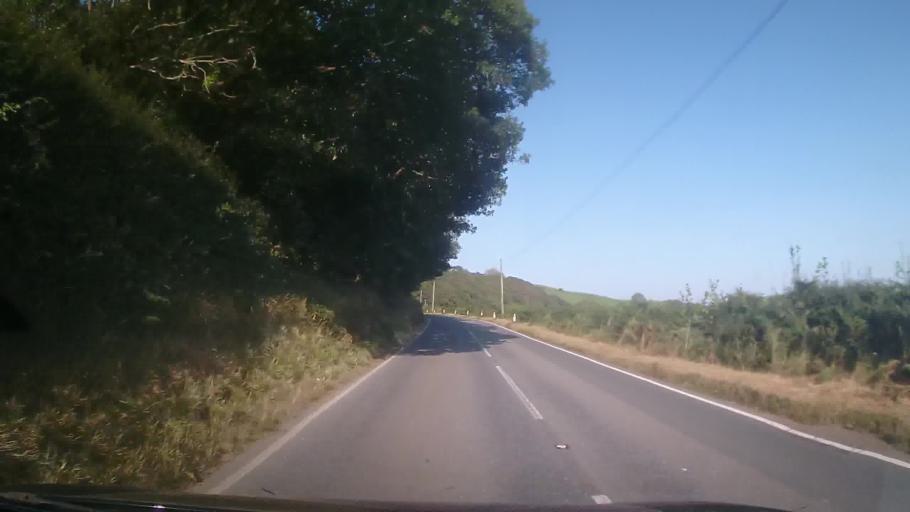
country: GB
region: Wales
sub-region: County of Ceredigion
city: Llangybi
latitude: 52.1396
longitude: -4.0730
